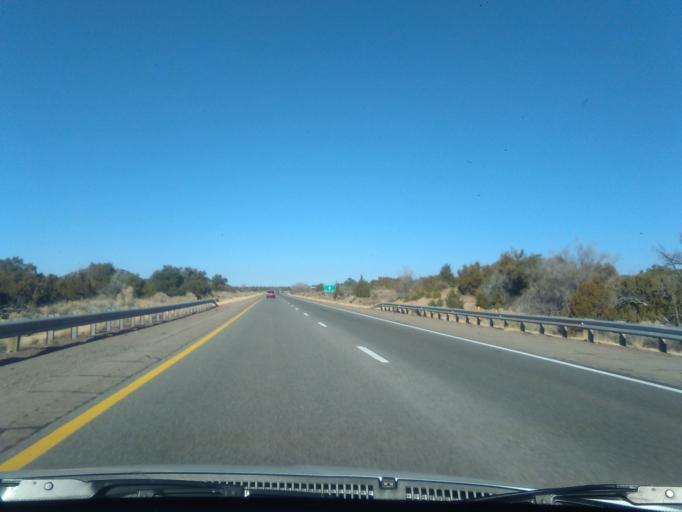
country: US
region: New Mexico
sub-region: Santa Fe County
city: Eldorado at Santa Fe
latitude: 35.5732
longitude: -105.8918
